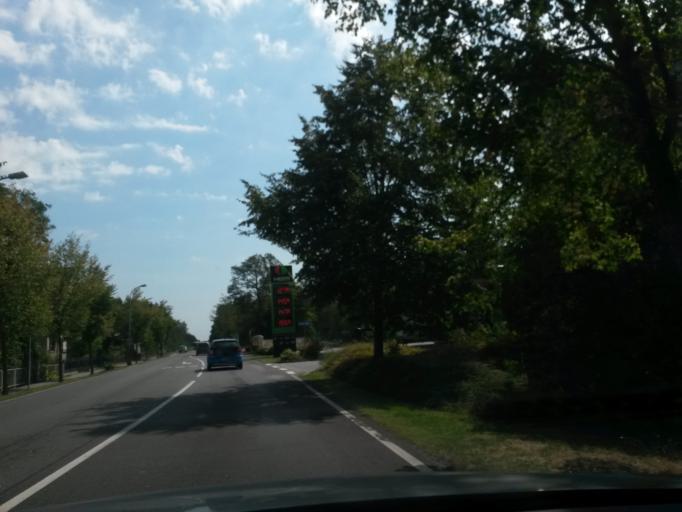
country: DE
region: Saxony-Anhalt
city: Jerichow
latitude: 52.4933
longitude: 12.0308
